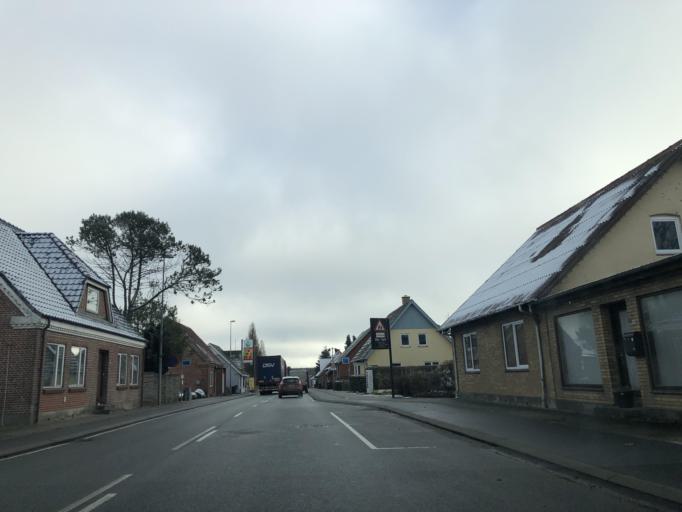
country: DK
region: Central Jutland
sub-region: Hedensted Kommune
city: Torring
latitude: 55.9315
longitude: 9.4907
